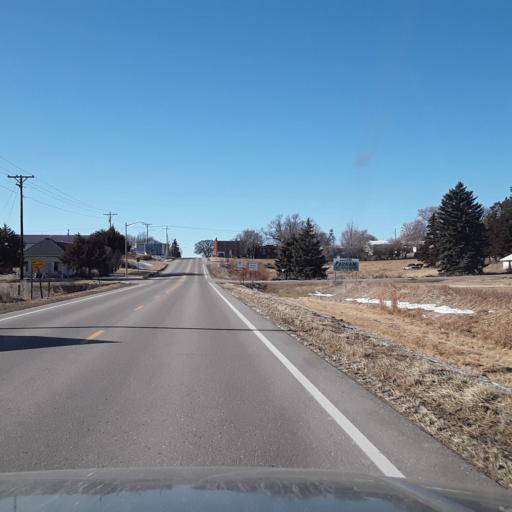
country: US
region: Nebraska
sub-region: Dawson County
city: Gothenburg
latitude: 40.7058
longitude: -100.2106
